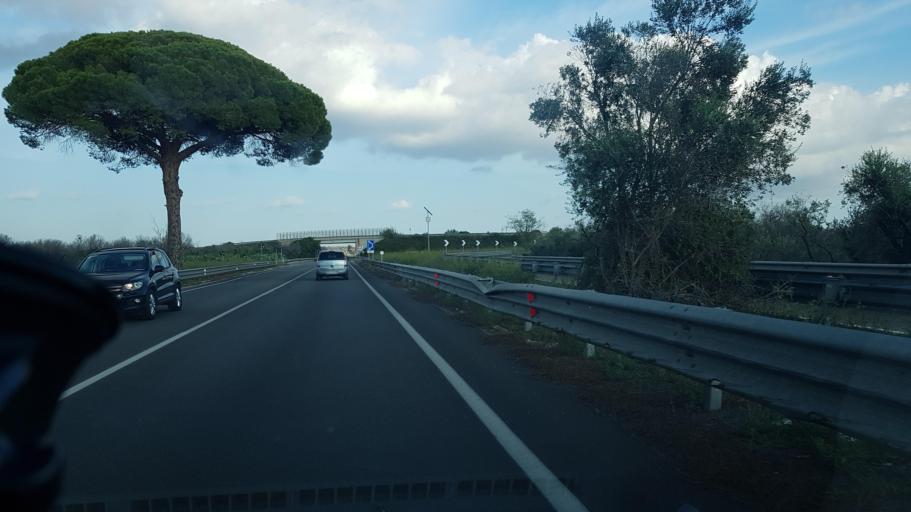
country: IT
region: Apulia
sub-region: Provincia di Lecce
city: Gemini
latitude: 39.9216
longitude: 18.1892
